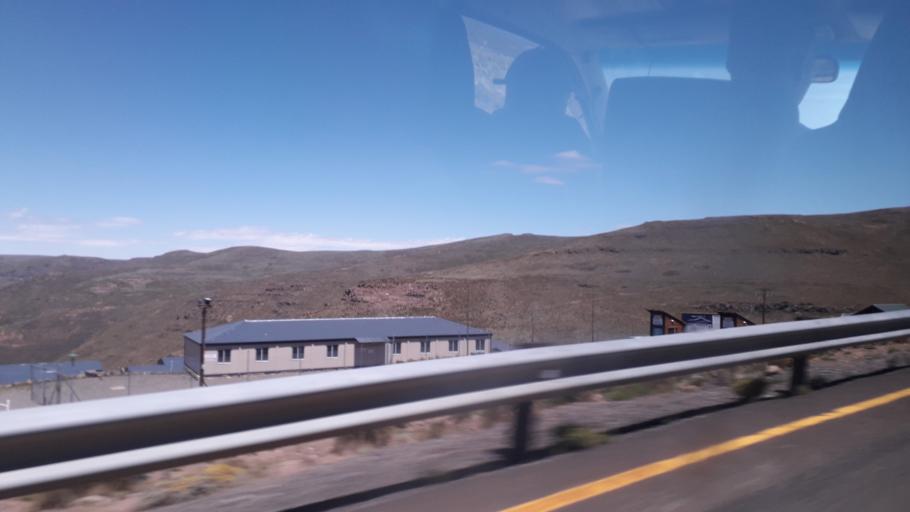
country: ZA
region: Orange Free State
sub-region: Thabo Mofutsanyana District Municipality
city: Phuthaditjhaba
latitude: -28.8293
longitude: 28.7306
